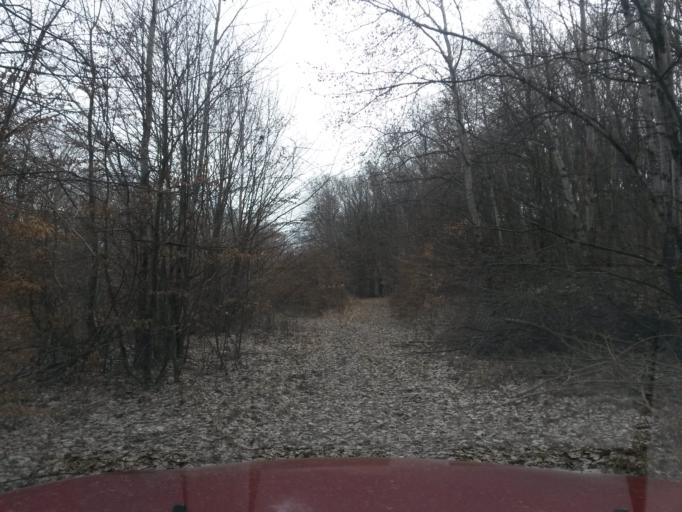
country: HU
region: Borsod-Abauj-Zemplen
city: Gonc
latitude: 48.5759
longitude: 21.3844
